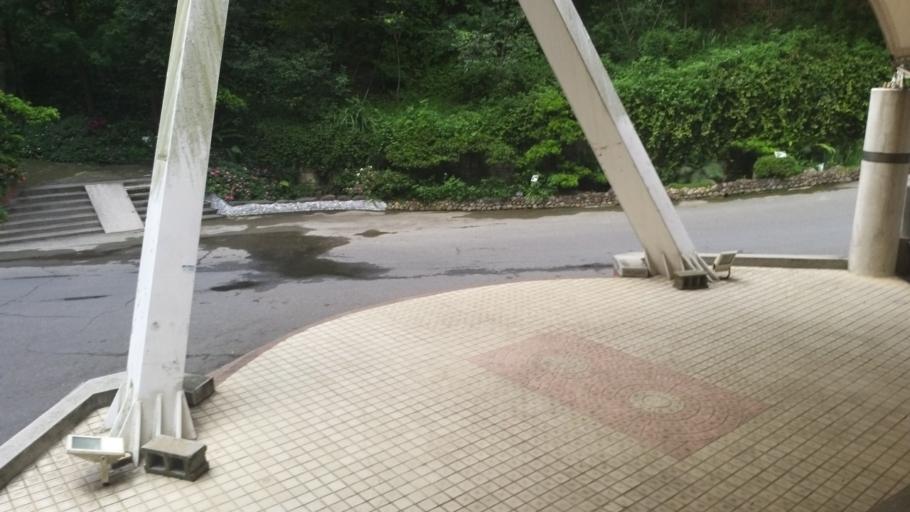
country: TW
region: Taiwan
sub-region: Changhua
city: Chang-hua
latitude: 24.0005
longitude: 120.5990
